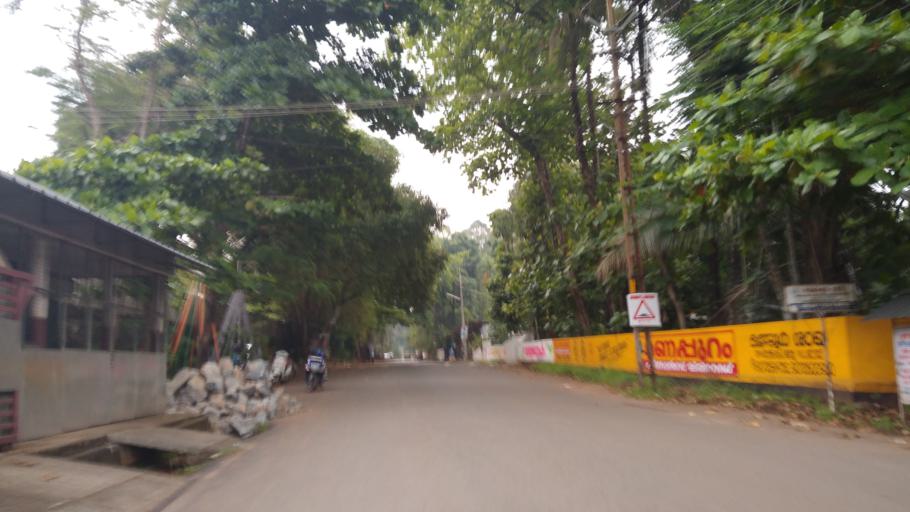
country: IN
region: Kerala
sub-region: Ernakulam
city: Perumbavoor
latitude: 10.0874
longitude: 76.5094
